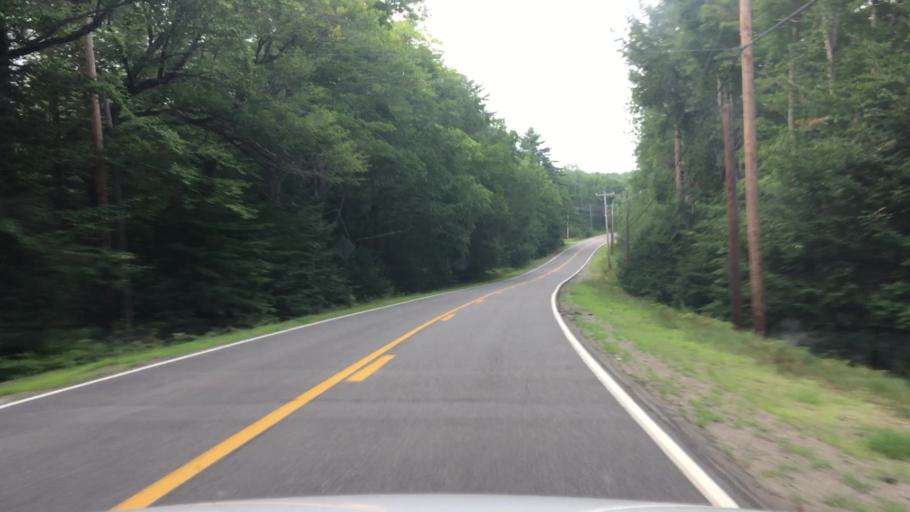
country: US
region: Maine
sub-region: Knox County
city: Washington
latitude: 44.2521
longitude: -69.3820
